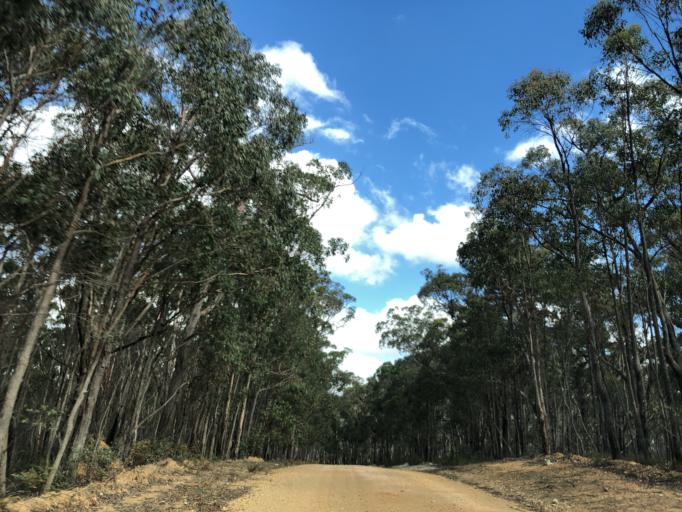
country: AU
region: Victoria
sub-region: Moorabool
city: Bacchus Marsh
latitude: -37.5345
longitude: 144.3329
